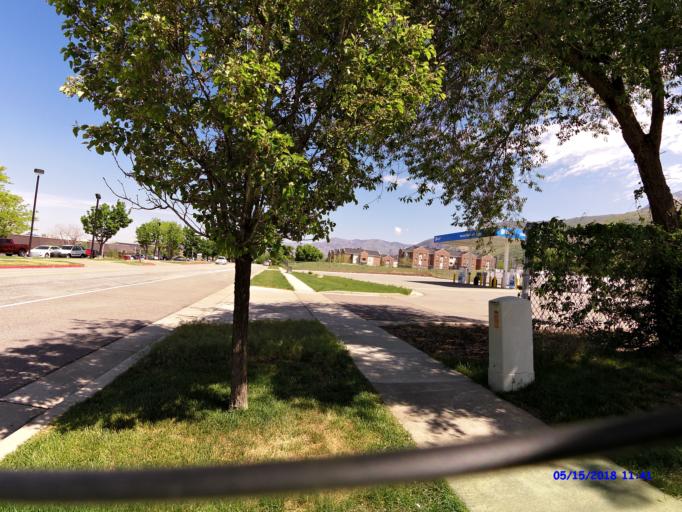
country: US
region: Utah
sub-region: Weber County
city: South Ogden
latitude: 41.1768
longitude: -111.9477
